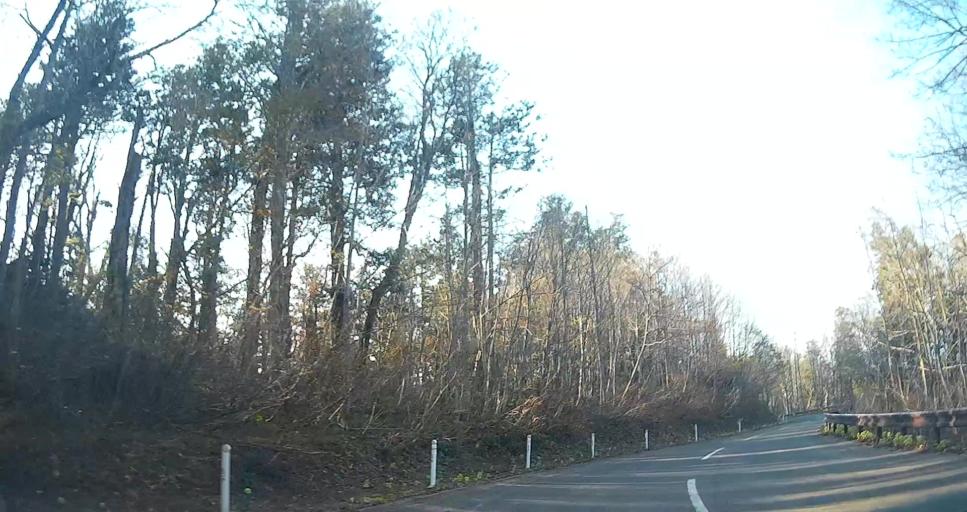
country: JP
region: Aomori
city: Mutsu
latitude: 41.3117
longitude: 141.1089
